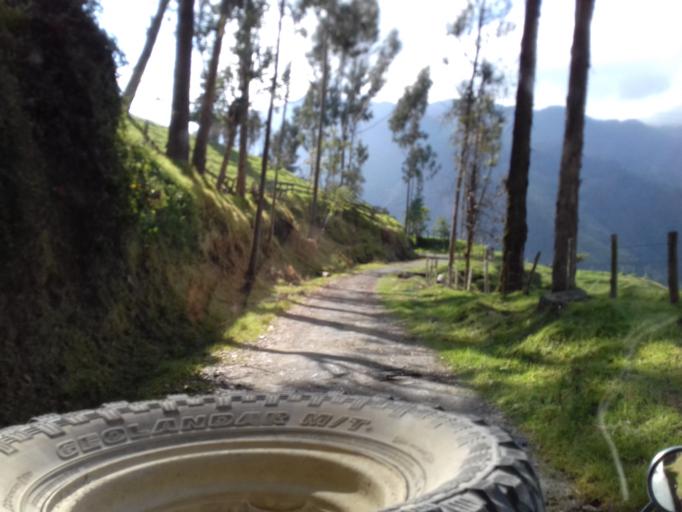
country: CO
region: Tolima
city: Cajamarca
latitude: 4.5306
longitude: -75.4472
